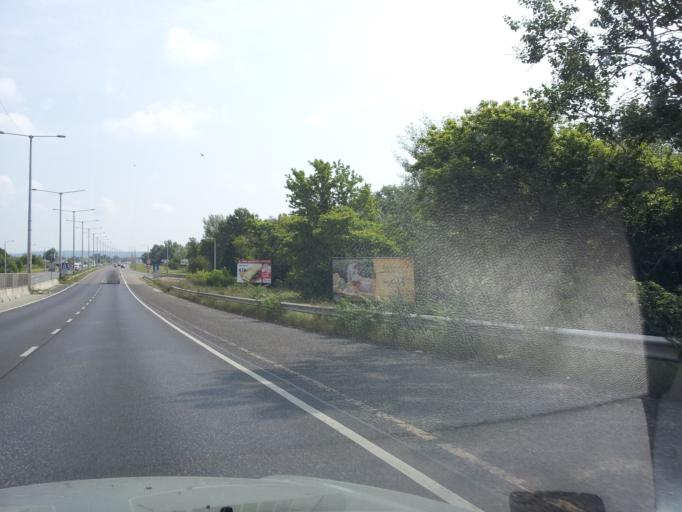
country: HU
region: Budapest
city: Budapest XV. keruelet
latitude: 47.5560
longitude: 19.1307
